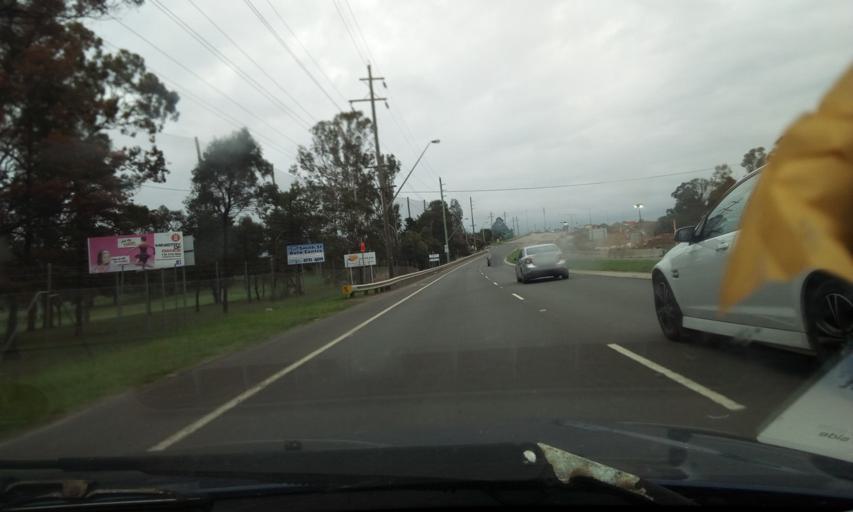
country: AU
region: New South Wales
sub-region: Penrith Municipality
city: Kingswood Park
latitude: -33.7901
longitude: 150.7001
